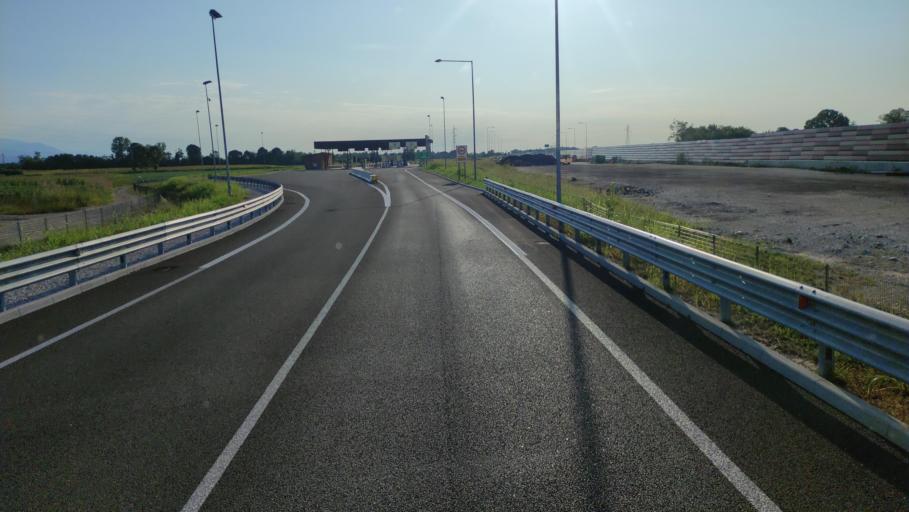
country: IT
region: Veneto
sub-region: Provincia di Vicenza
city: Isola Vicentina
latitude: 45.6488
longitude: 11.4398
